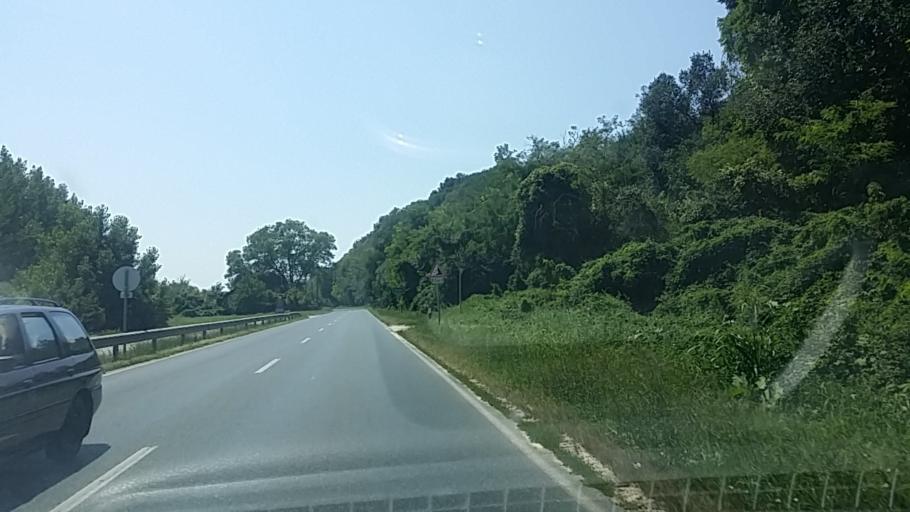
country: HU
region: Tolna
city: Paks
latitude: 46.6461
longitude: 18.8804
